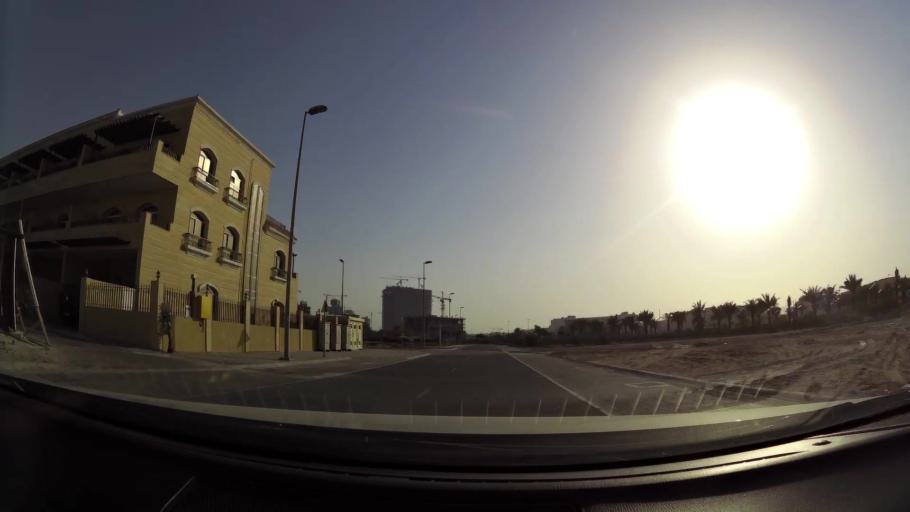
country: AE
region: Dubai
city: Dubai
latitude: 25.0609
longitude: 55.2130
